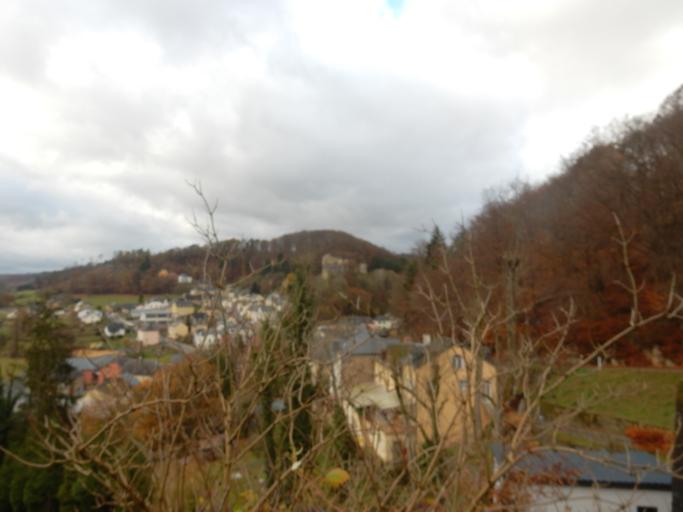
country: LU
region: Luxembourg
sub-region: Canton de Capellen
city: Septfontaines
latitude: 49.7013
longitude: 5.9695
